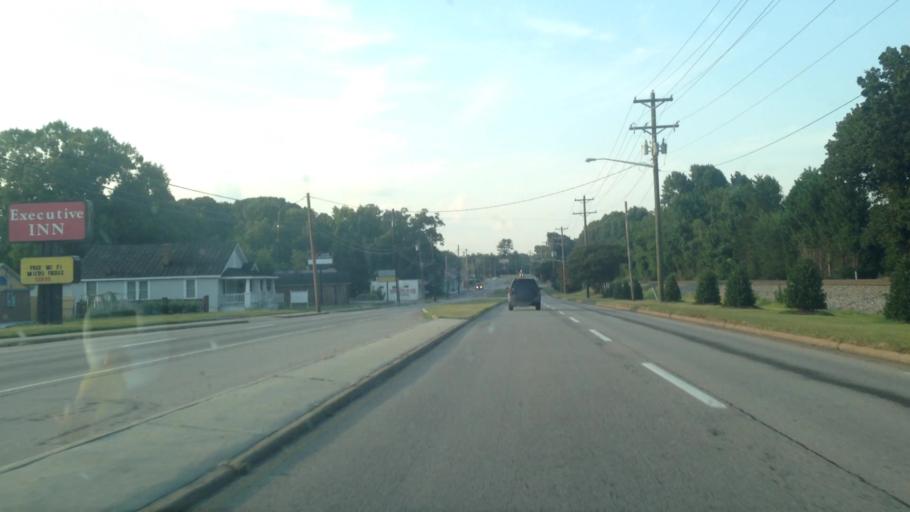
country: US
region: Virginia
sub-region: City of Danville
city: Danville
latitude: 36.5546
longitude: -79.4590
